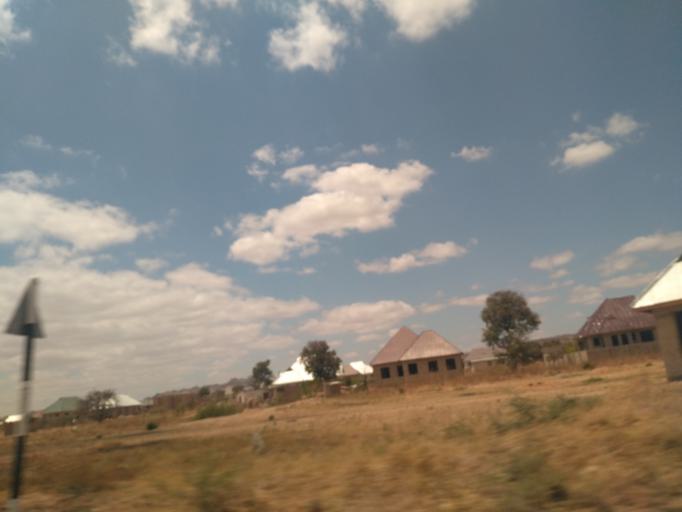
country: TZ
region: Dodoma
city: Kisasa
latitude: -6.1713
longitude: 35.7906
